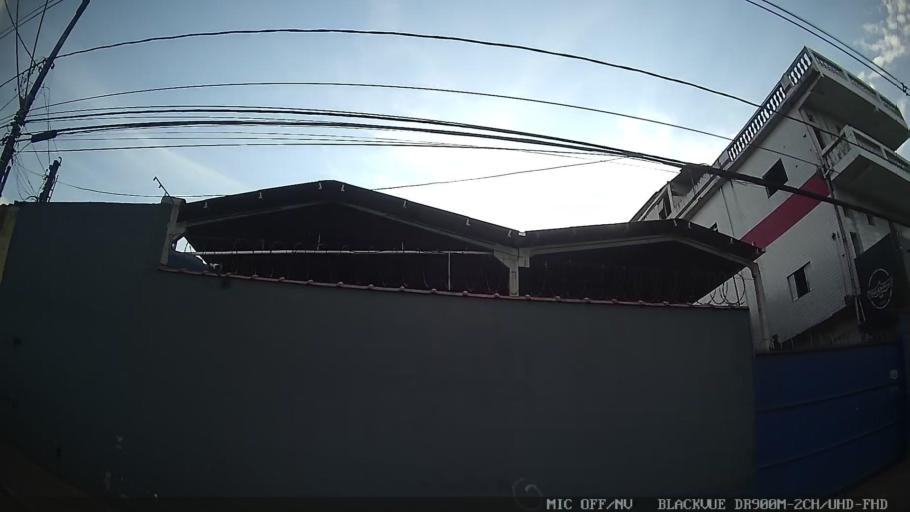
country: BR
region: Sao Paulo
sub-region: Cubatao
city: Cubatao
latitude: -23.9010
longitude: -46.4226
